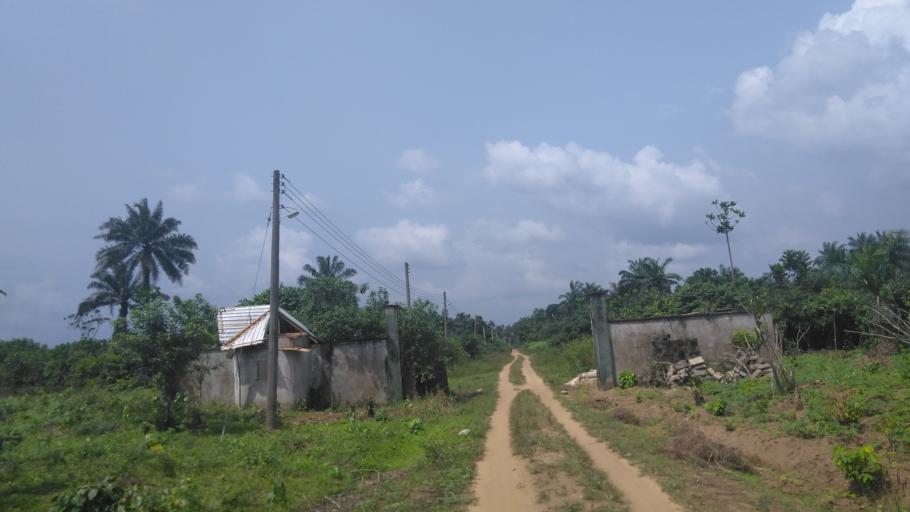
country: NG
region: Abia
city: Aba
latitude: 5.0420
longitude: 7.2369
